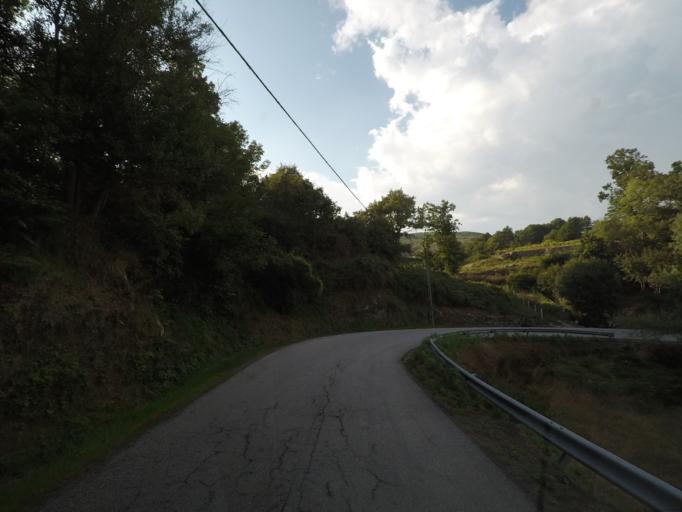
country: PT
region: Porto
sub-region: Baiao
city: Valadares
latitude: 41.1780
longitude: -7.9415
